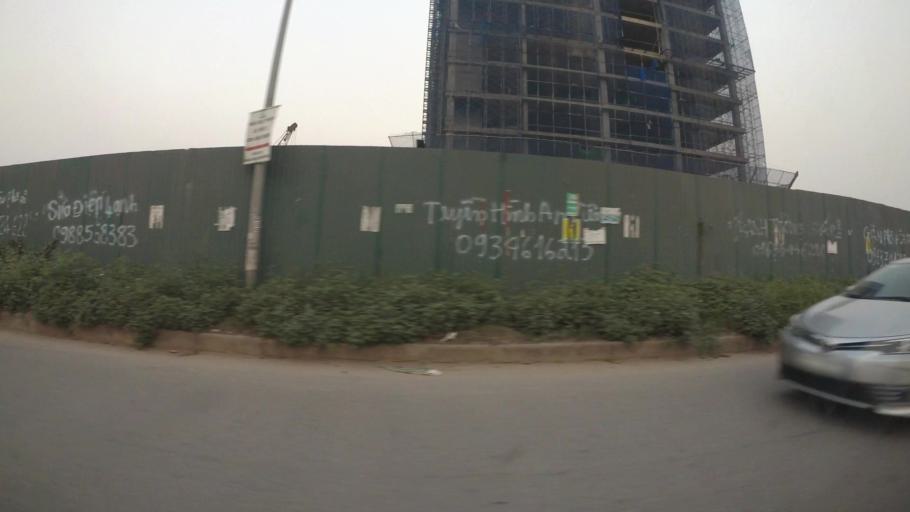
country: VN
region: Ha Noi
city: Tay Ho
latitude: 21.0643
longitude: 105.7899
